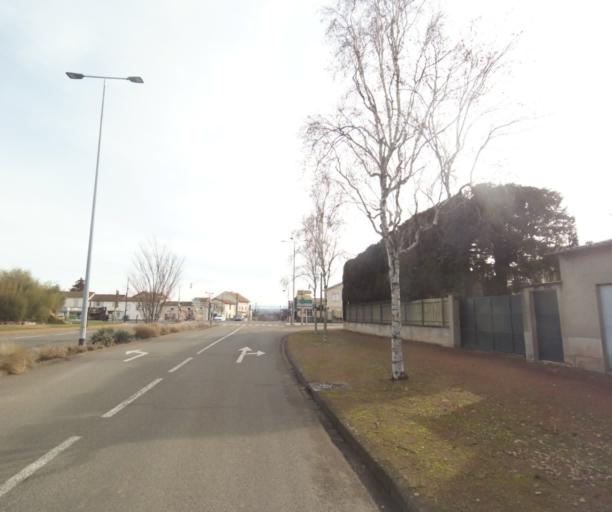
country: FR
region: Rhone-Alpes
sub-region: Departement de la Loire
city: Roanne
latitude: 46.0250
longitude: 4.0571
